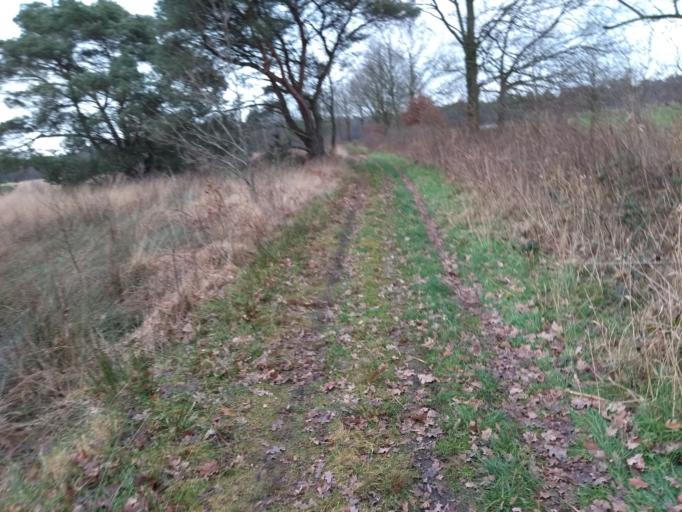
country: NL
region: Overijssel
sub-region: Gemeente Twenterand
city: Magele
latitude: 52.5035
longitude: 6.5464
